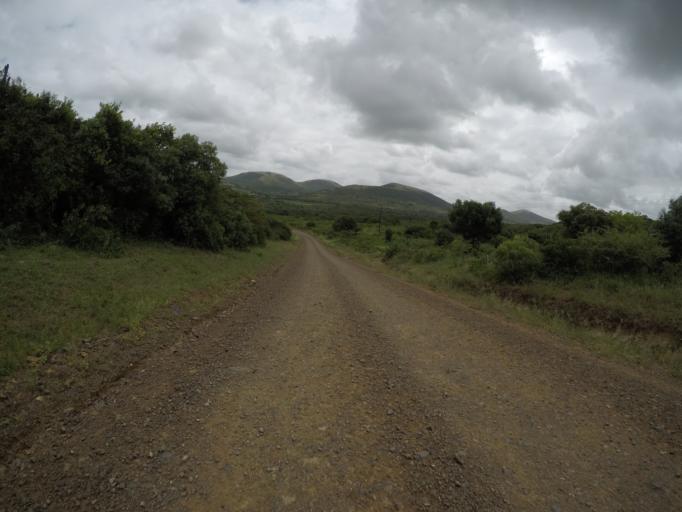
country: ZA
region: KwaZulu-Natal
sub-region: uThungulu District Municipality
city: Empangeni
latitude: -28.6002
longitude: 31.8936
